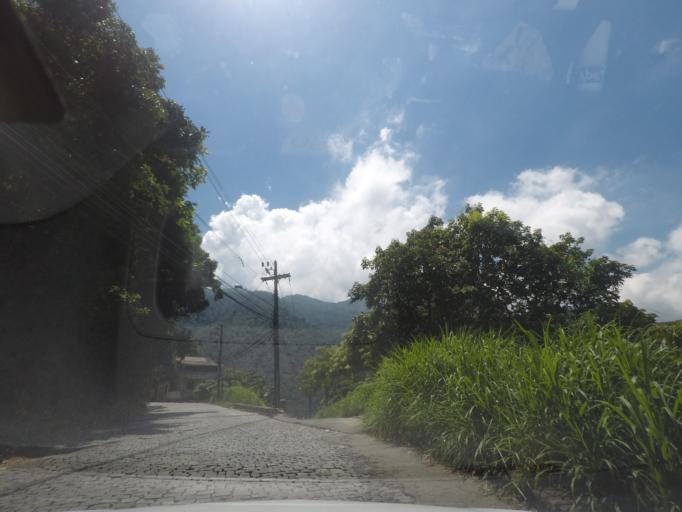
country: BR
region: Rio de Janeiro
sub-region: Petropolis
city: Petropolis
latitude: -22.5353
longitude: -43.1724
